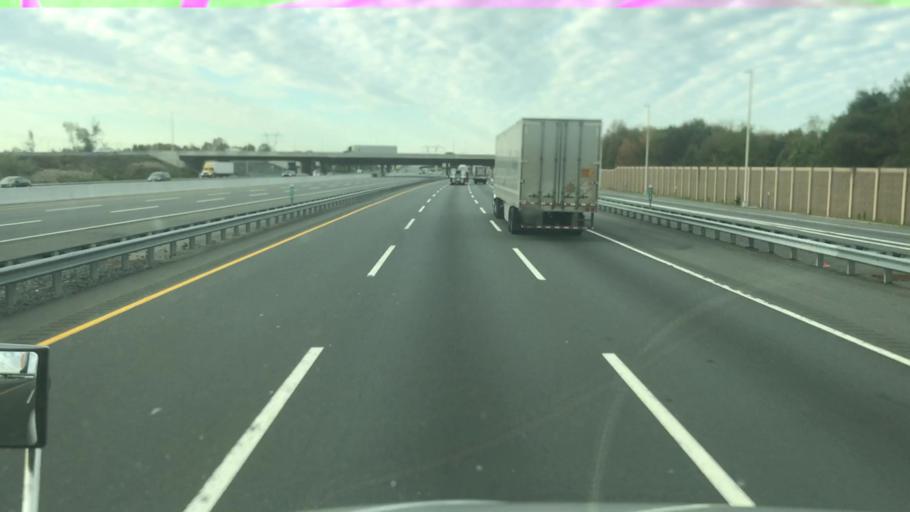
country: US
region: New Jersey
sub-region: Monmouth County
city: Allentown
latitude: 40.1958
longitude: -74.5983
